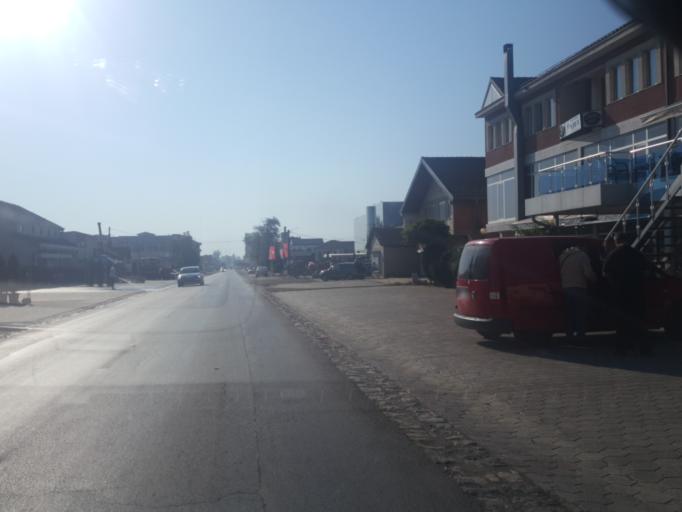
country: XK
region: Gjakova
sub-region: Komuna e Gjakoves
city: Gjakove
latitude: 42.4063
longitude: 20.4087
